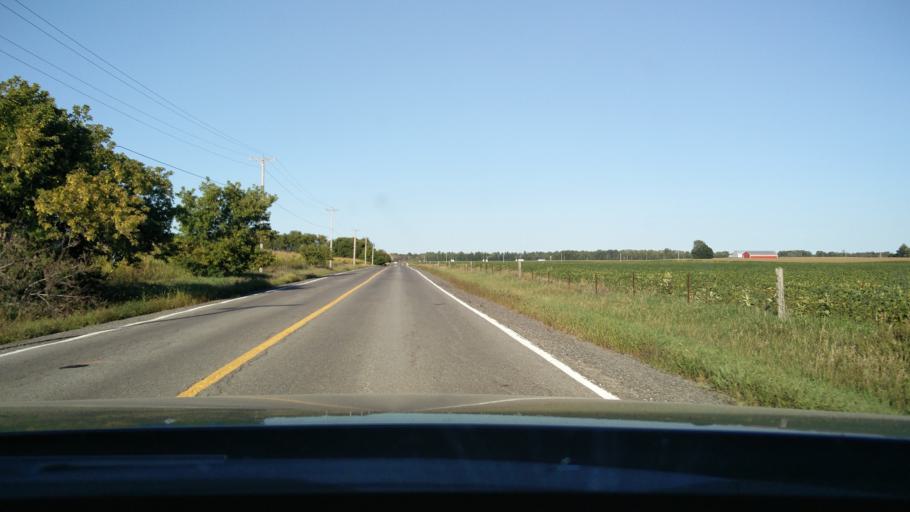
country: CA
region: Ontario
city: Bells Corners
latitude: 45.2103
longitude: -75.7899
